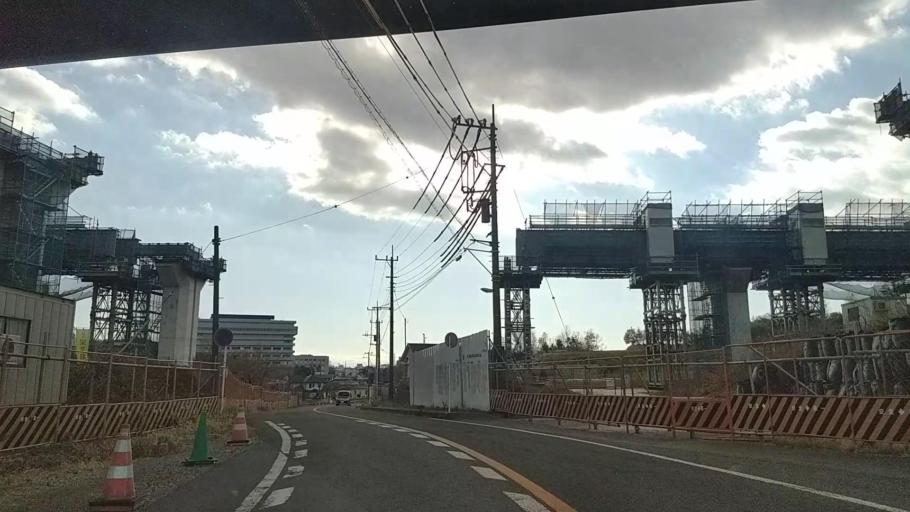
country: JP
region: Kanagawa
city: Isehara
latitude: 35.4114
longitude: 139.3135
